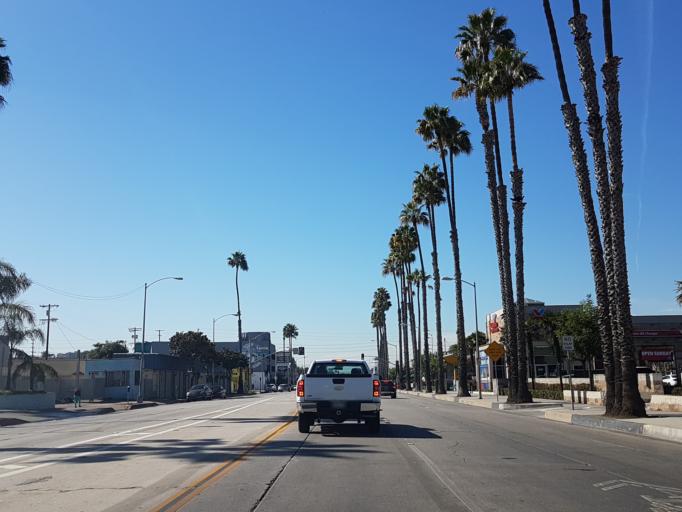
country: US
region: California
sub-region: Los Angeles County
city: Marina del Rey
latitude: 33.9919
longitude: -118.4449
